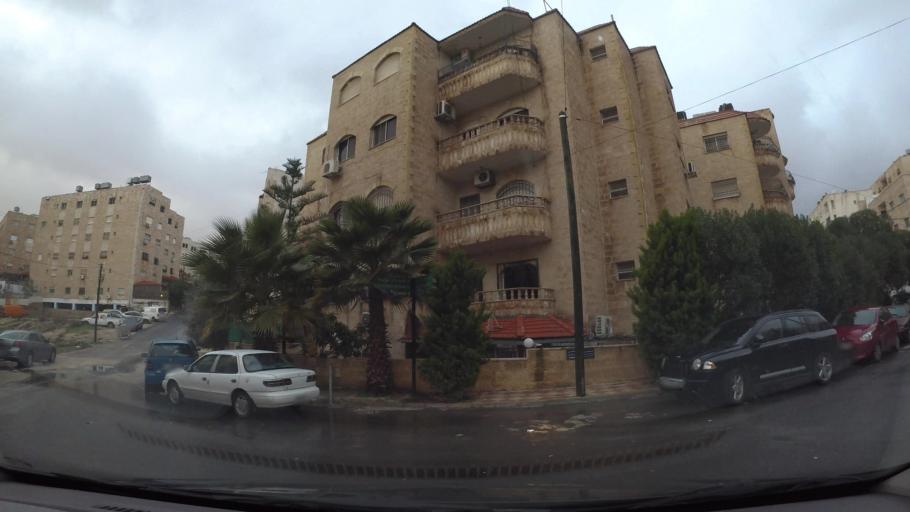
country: JO
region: Amman
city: Amman
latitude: 32.0037
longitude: 35.9321
